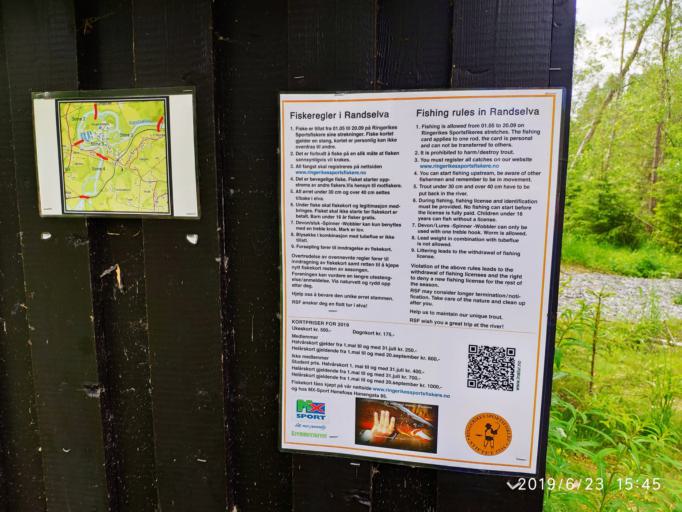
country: NO
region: Buskerud
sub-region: Ringerike
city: Honefoss
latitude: 60.1962
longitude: 10.3013
